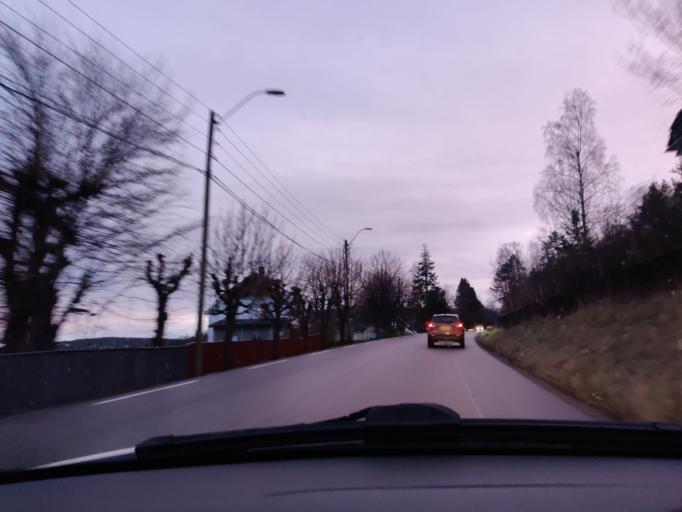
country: NO
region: Vestfold
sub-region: Tonsberg
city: Sem
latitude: 59.2735
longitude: 10.3658
